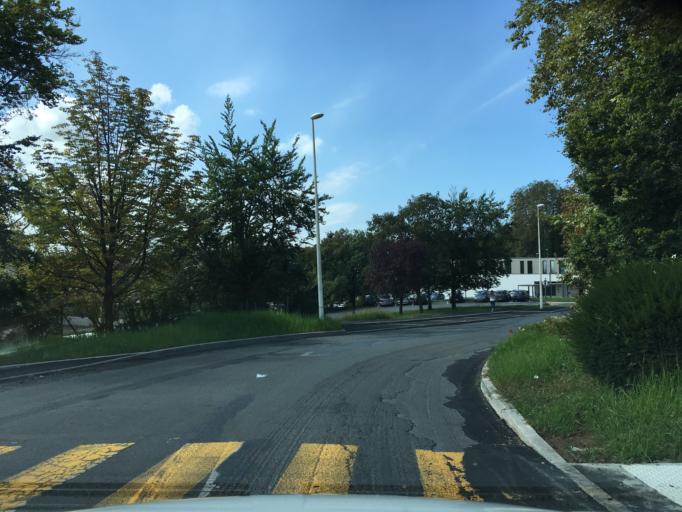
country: FR
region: Aquitaine
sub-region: Departement des Pyrenees-Atlantiques
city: Boucau
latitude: 43.5000
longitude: -1.4565
